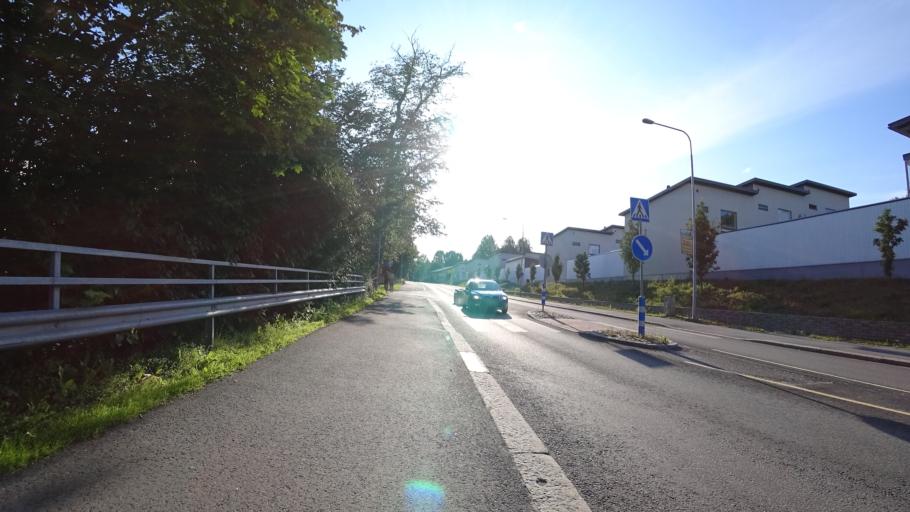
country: FI
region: Pirkanmaa
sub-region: Tampere
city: Pirkkala
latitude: 61.5088
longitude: 23.6800
